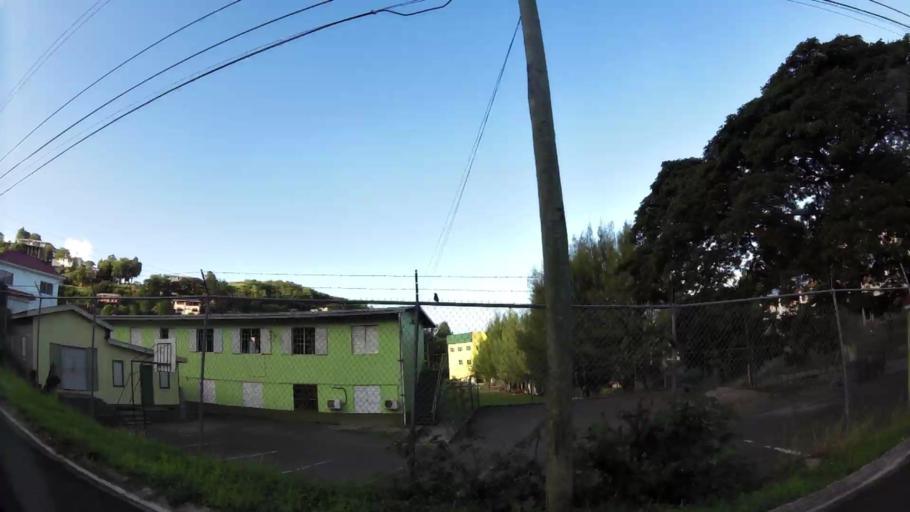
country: LC
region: Castries Quarter
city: Bisee
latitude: 14.0294
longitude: -60.9742
